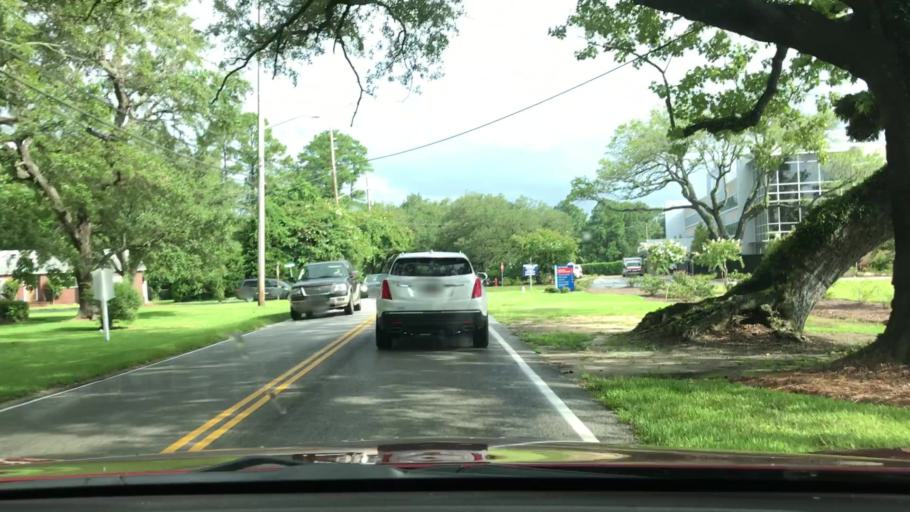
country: US
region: South Carolina
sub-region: Georgetown County
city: Georgetown
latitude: 33.3785
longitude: -79.2851
